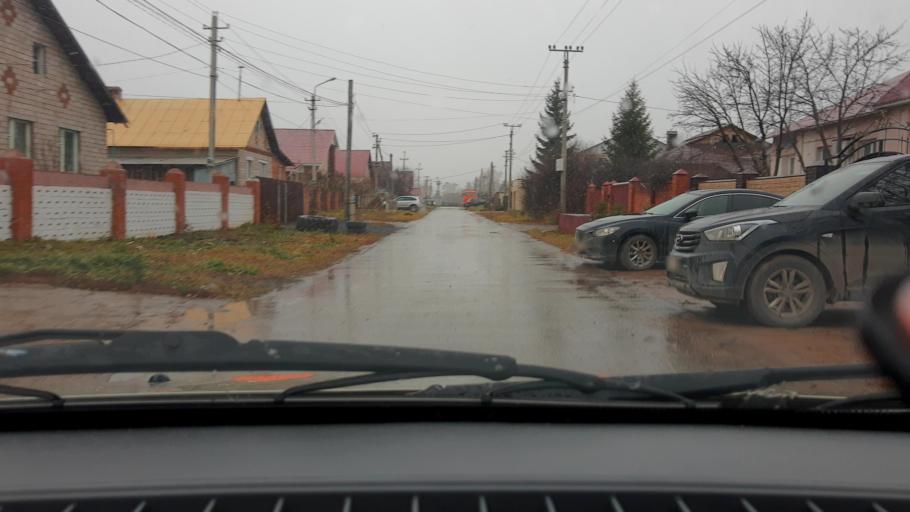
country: RU
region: Bashkortostan
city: Ufa
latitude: 54.6204
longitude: 55.9120
